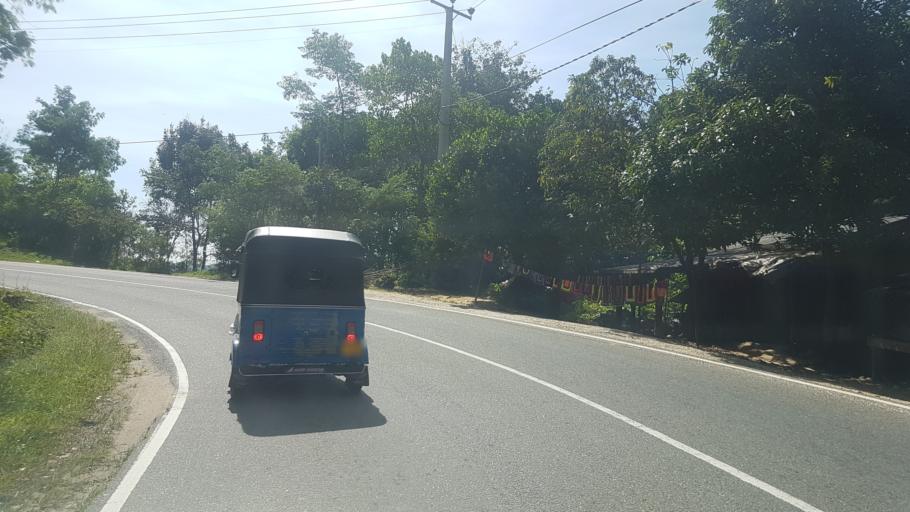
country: LK
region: Uva
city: Haputale
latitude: 6.8030
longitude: 81.0869
